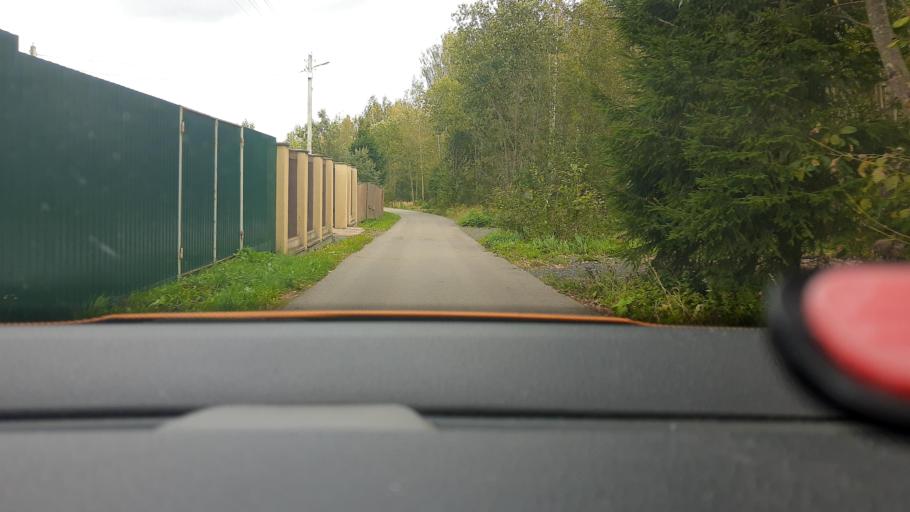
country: RU
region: Moskovskaya
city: Ashukino
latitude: 56.0883
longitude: 38.0244
